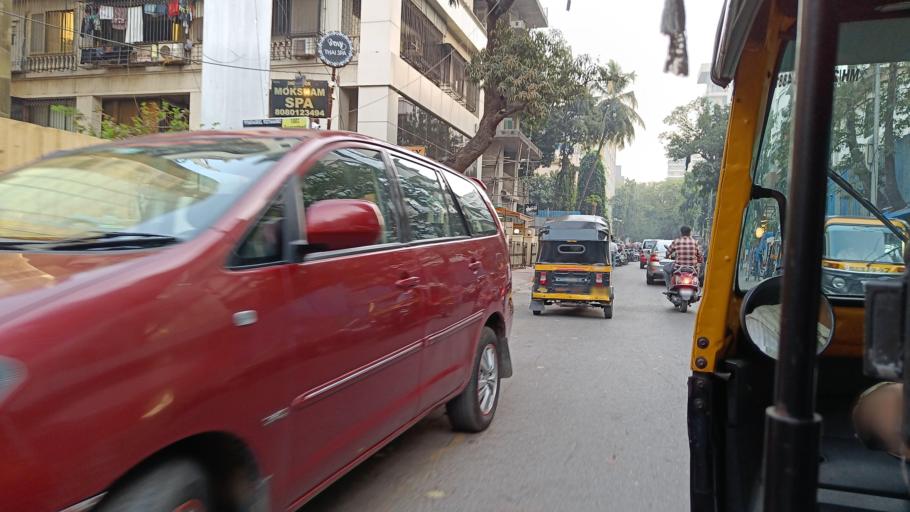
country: IN
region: Maharashtra
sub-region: Mumbai Suburban
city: Mumbai
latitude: 19.0665
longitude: 72.8335
